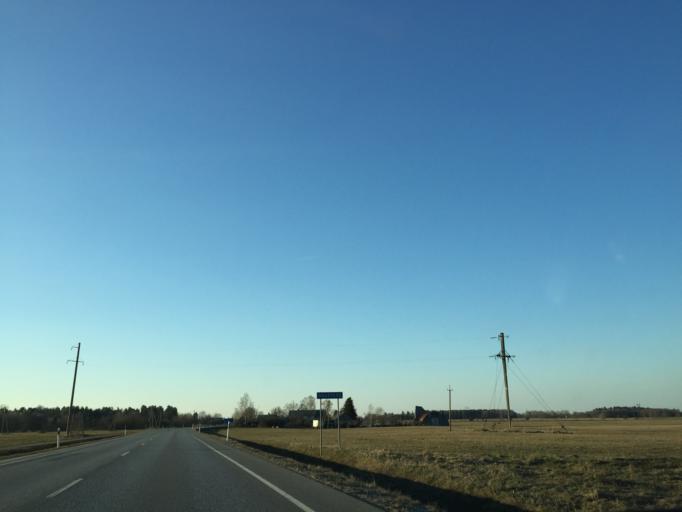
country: EE
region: Ida-Virumaa
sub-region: Johvi vald
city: Johvi
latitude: 59.2889
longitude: 27.4968
